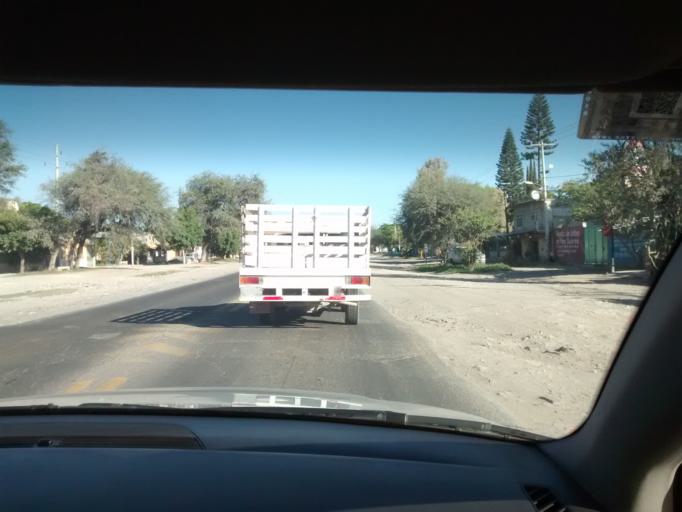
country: MX
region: Puebla
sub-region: Tehuacan
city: Magdalena Cuayucatepec
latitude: 18.5104
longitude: -97.4913
